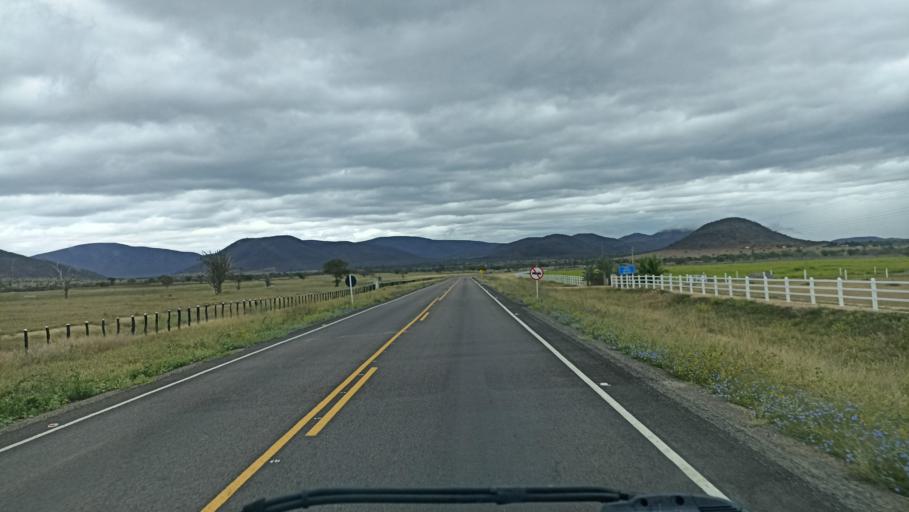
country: BR
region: Bahia
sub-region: Iacu
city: Iacu
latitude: -12.9188
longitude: -40.4134
